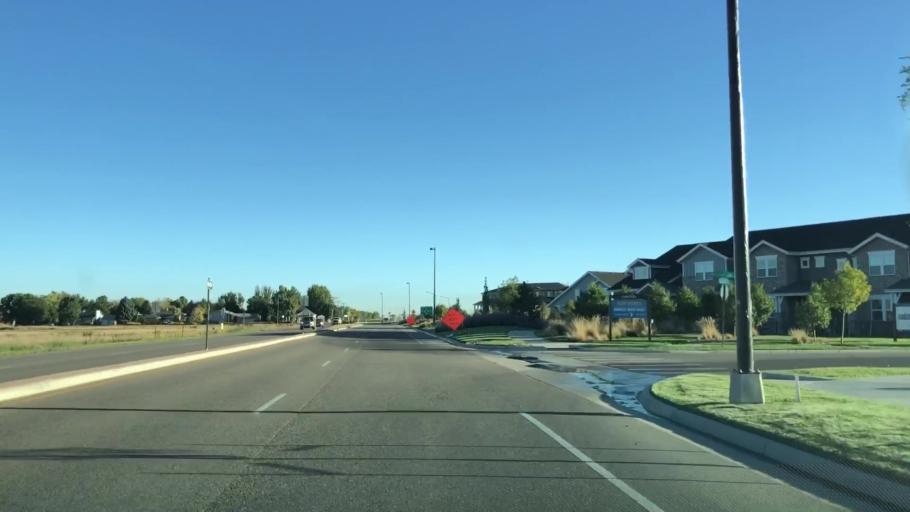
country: US
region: Colorado
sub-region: Larimer County
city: Loveland
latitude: 40.4166
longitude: -105.0209
